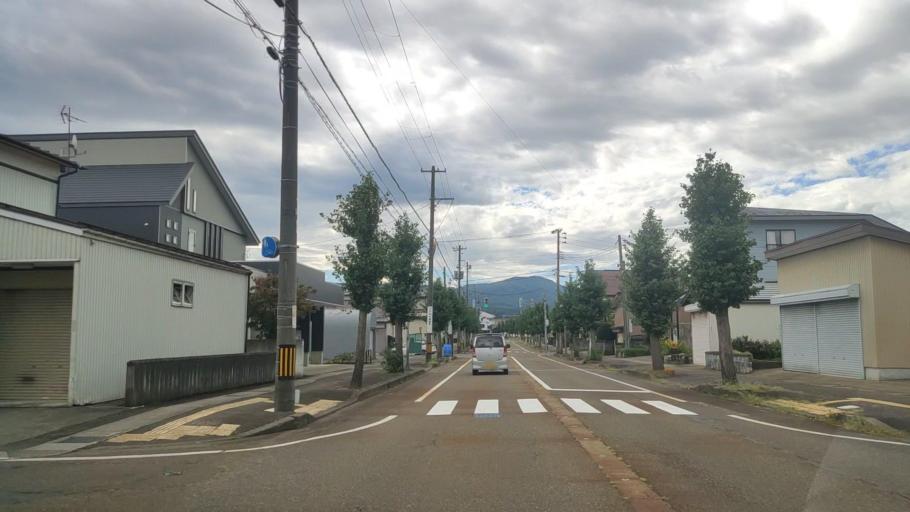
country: JP
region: Niigata
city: Arai
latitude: 37.0236
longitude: 138.2463
